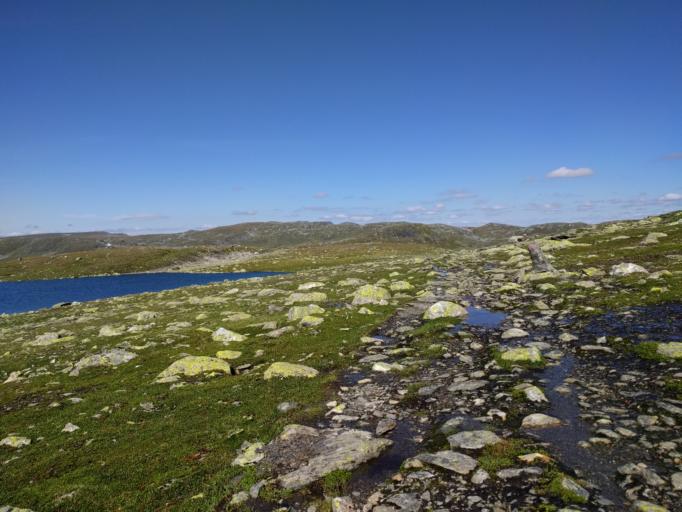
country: NO
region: Aust-Agder
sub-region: Bykle
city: Hovden
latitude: 59.8891
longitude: 7.2082
